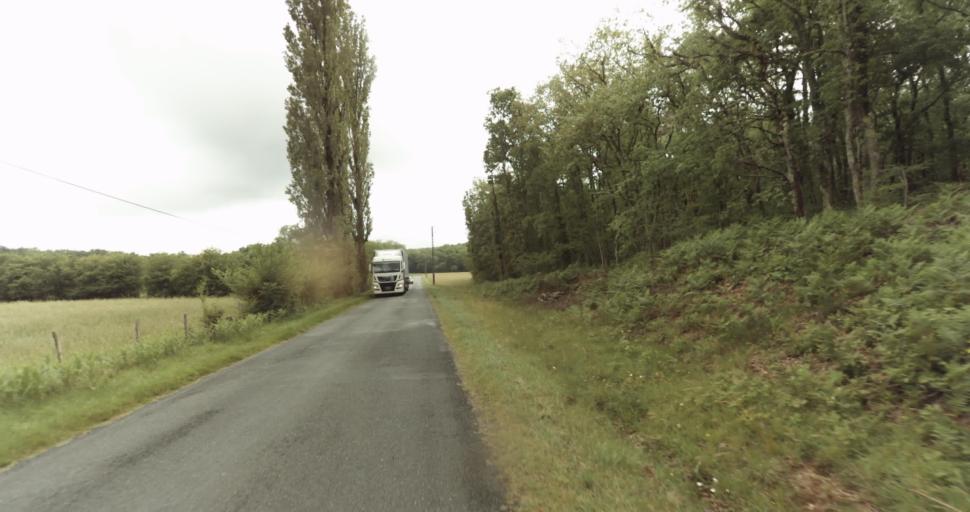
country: FR
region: Aquitaine
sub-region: Departement de la Dordogne
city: Belves
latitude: 44.7525
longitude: 0.9569
